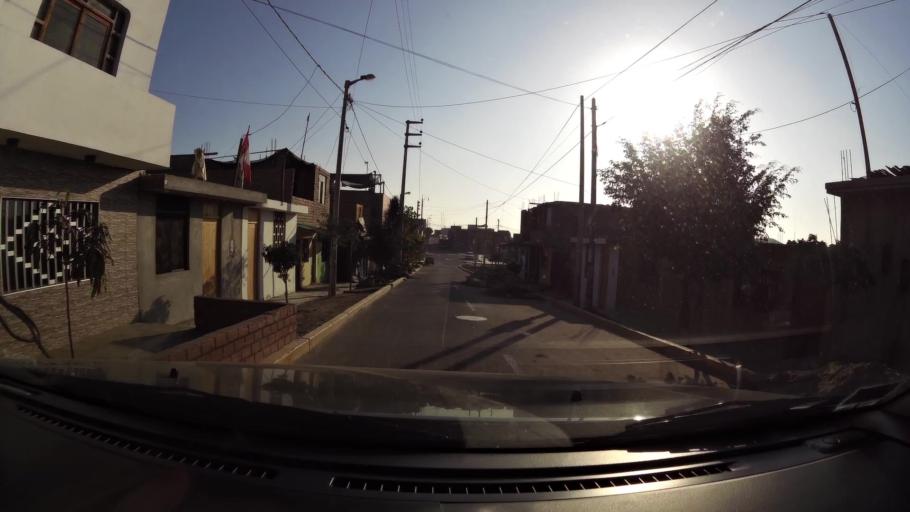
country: PE
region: Ica
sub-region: Provincia de Pisco
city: Villa Tupac Amaru
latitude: -13.7054
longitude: -76.1486
